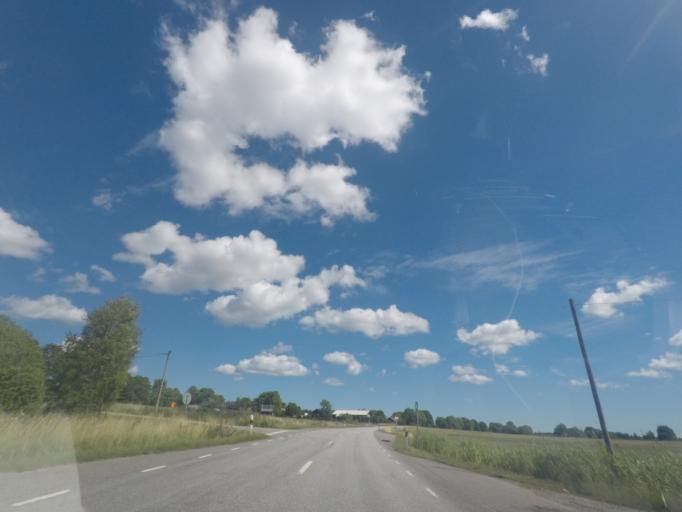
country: SE
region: Stockholm
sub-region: Norrtalje Kommun
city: Hallstavik
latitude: 59.9560
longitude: 18.7842
